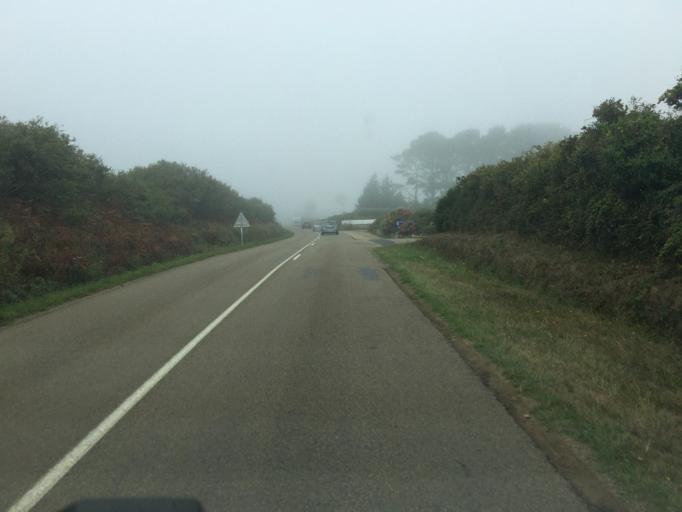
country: FR
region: Brittany
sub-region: Departement du Finistere
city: Plogoff
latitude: 48.0566
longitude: -4.6726
